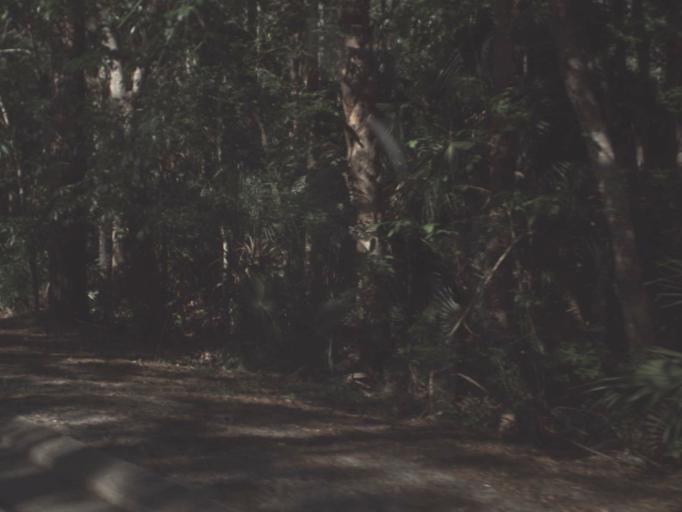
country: US
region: Florida
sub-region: Flagler County
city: Palm Coast
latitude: 29.5636
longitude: -81.1912
